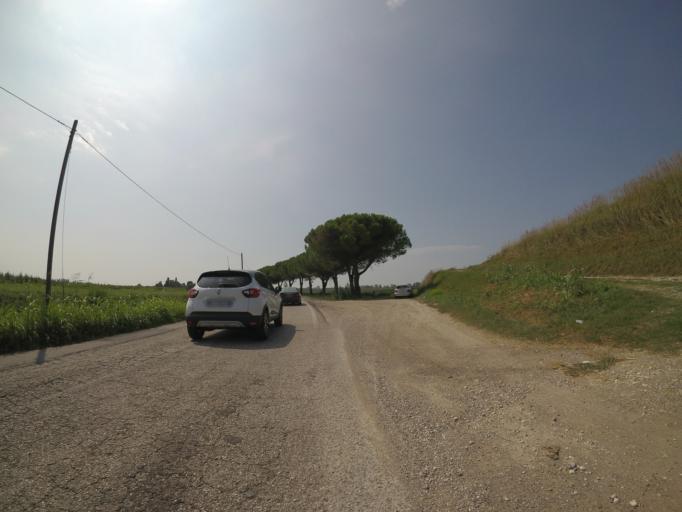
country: IT
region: Friuli Venezia Giulia
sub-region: Provincia di Udine
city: Pertegada
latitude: 45.6909
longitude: 13.0552
